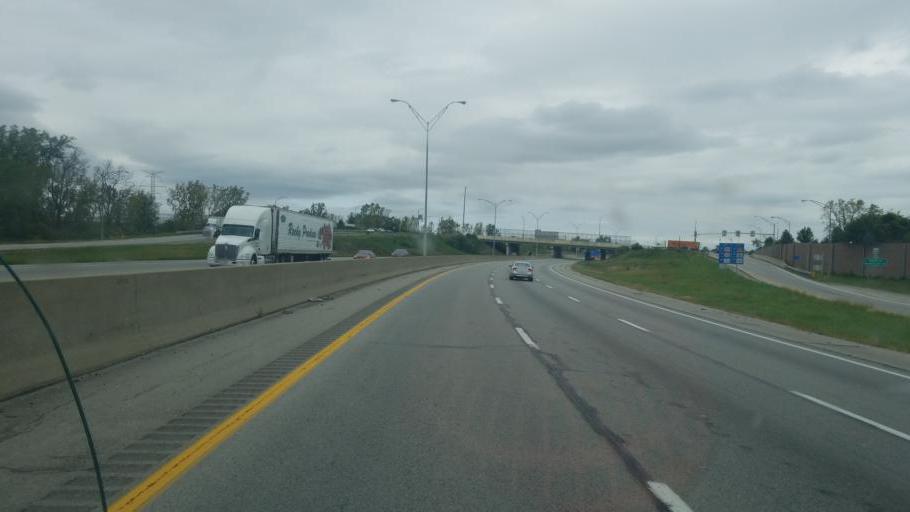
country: US
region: Ohio
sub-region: Lucas County
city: Toledo
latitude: 41.7188
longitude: -83.5021
